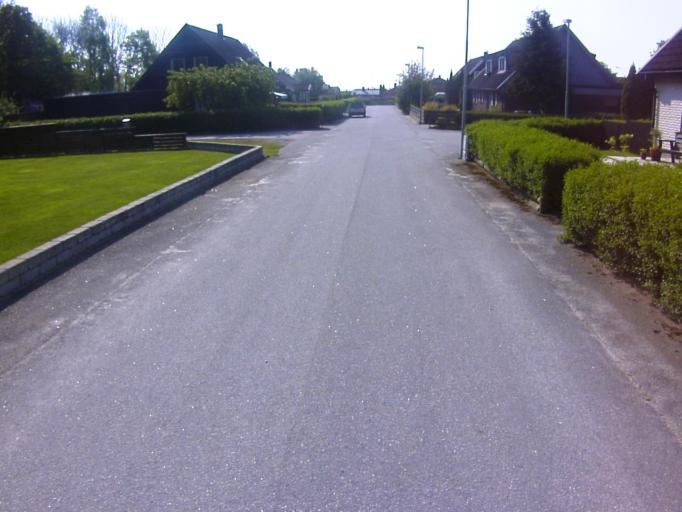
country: SE
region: Blekinge
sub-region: Solvesborgs Kommun
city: Soelvesborg
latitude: 56.0087
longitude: 14.7328
